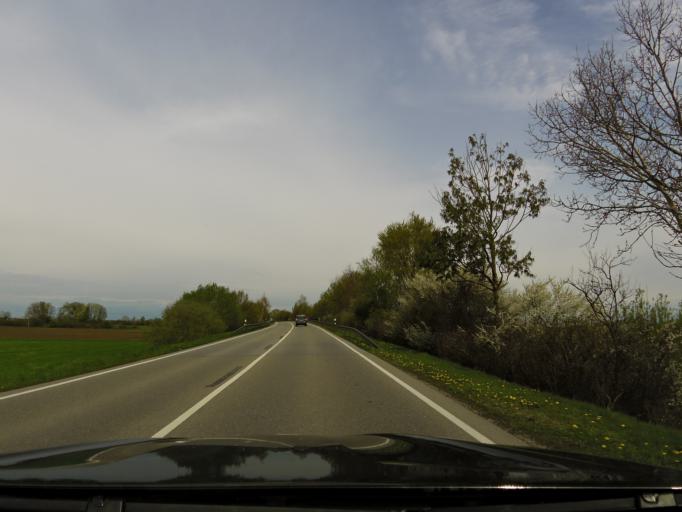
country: DE
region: Bavaria
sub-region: Upper Bavaria
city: Oberding
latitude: 48.3285
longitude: 11.8781
